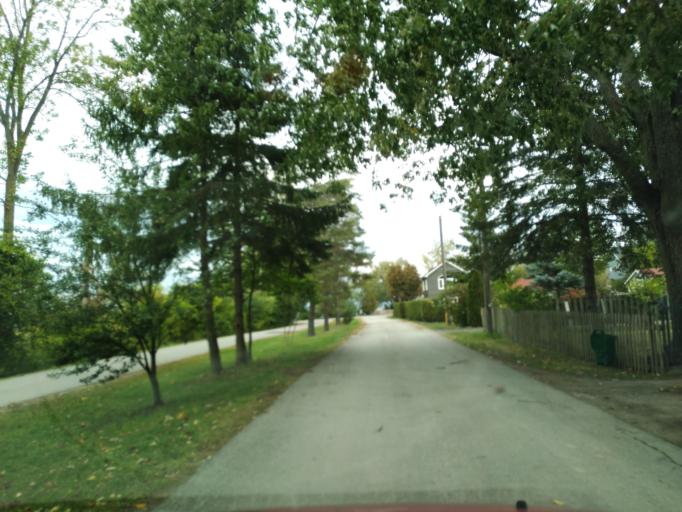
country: CA
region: Ontario
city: Keswick
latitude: 44.3133
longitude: -79.4197
